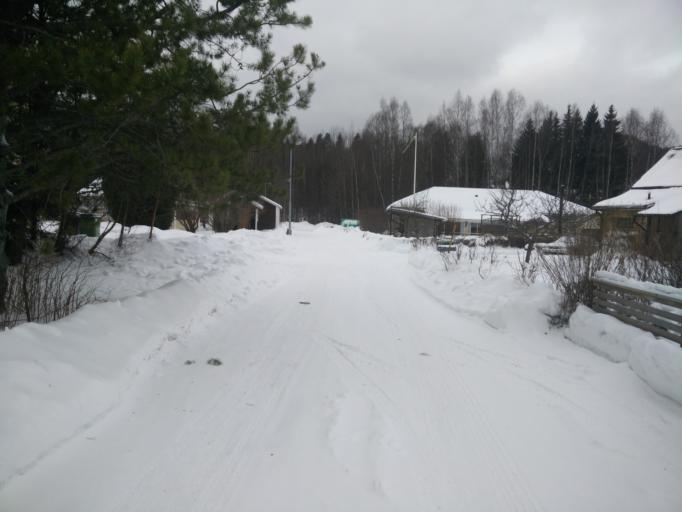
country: SE
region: Vaesternorrland
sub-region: Sundsvalls Kommun
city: Kvissleby
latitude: 62.2923
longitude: 17.3758
